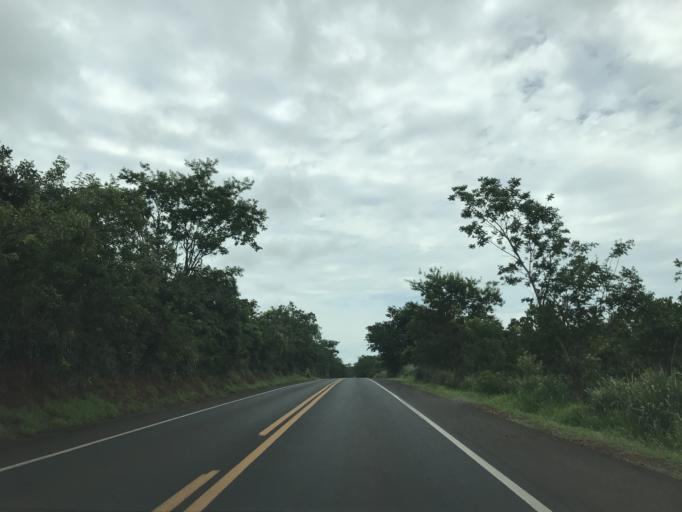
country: BR
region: Minas Gerais
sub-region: Frutal
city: Frutal
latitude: -19.8936
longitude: -48.9718
